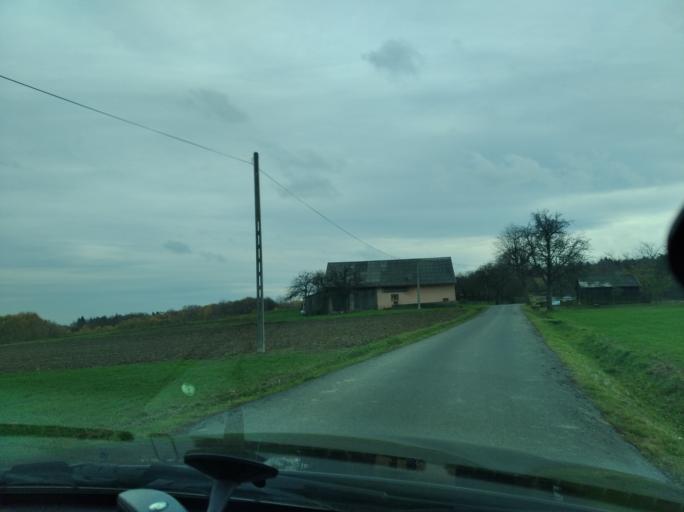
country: PL
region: Subcarpathian Voivodeship
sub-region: Powiat strzyzowski
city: Strzyzow
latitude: 49.9129
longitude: 21.7714
